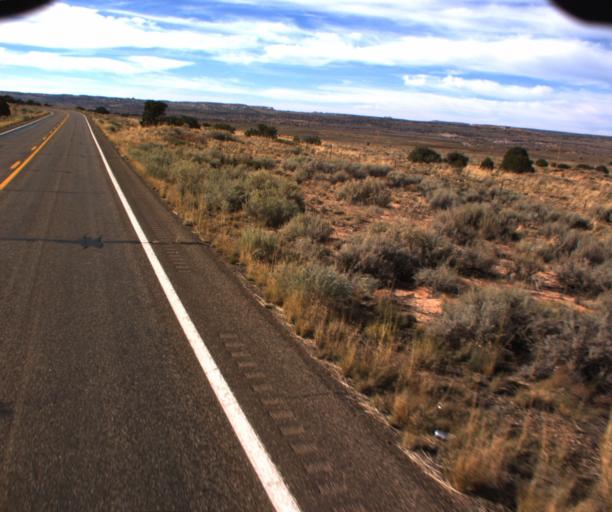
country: US
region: Arizona
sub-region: Coconino County
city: Kaibito
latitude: 36.6763
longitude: -111.2561
